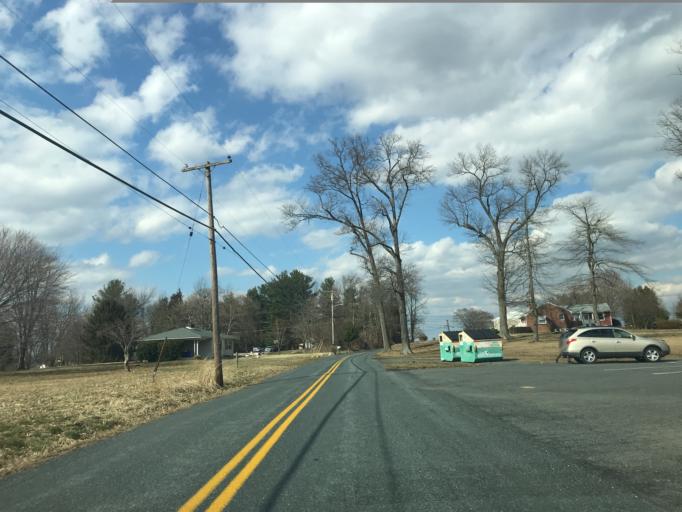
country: US
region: Maryland
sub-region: Harford County
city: Aberdeen
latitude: 39.5801
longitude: -76.1989
